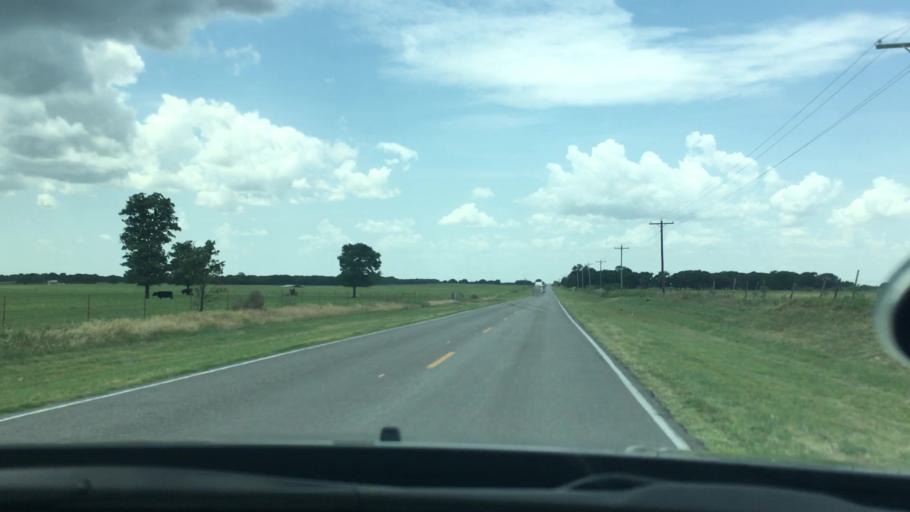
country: US
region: Oklahoma
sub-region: Carter County
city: Wilson
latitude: 33.9403
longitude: -97.3941
